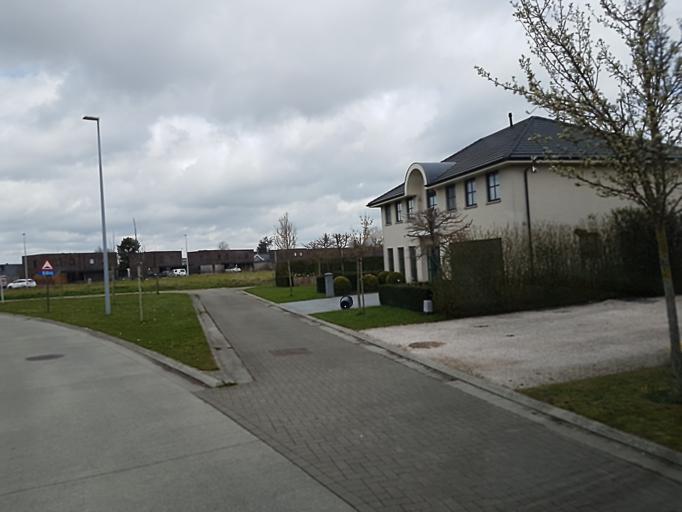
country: BE
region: Flanders
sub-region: Provincie Oost-Vlaanderen
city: Deinze
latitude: 50.9652
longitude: 3.5260
